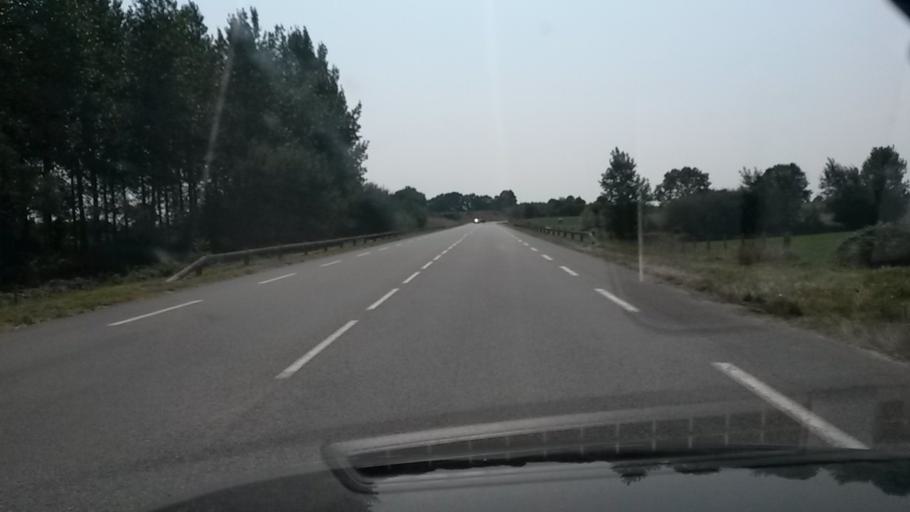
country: FR
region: Pays de la Loire
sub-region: Departement de la Mayenne
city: Chemaze
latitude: 47.7872
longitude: -0.7641
